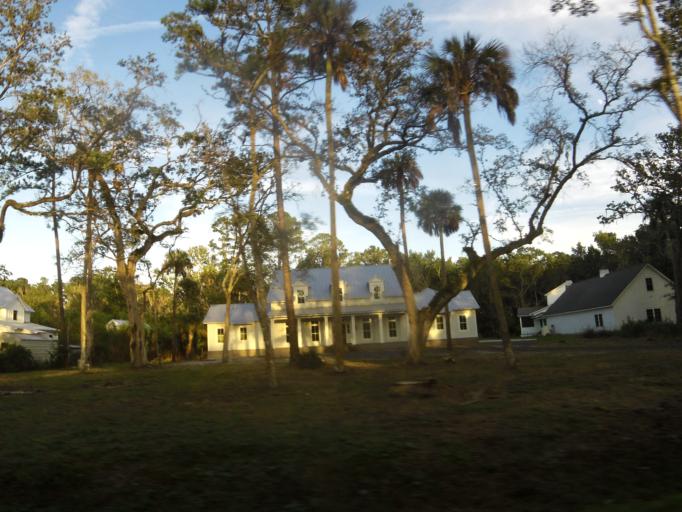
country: US
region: Florida
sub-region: Saint Johns County
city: Palm Valley
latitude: 30.1824
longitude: -81.3968
